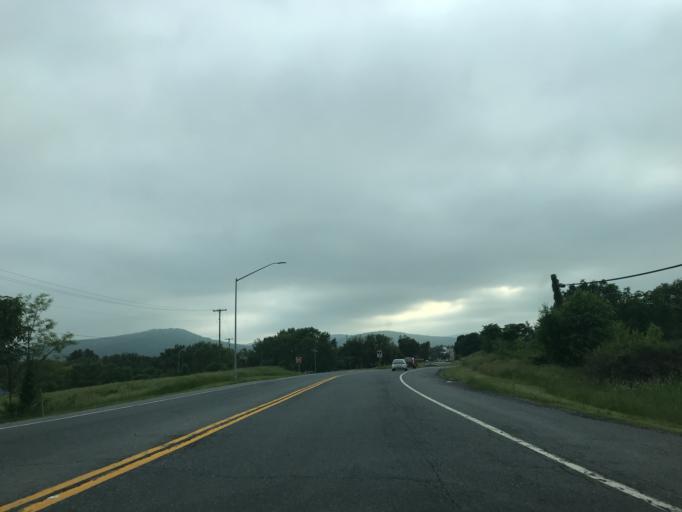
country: US
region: Maryland
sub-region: Frederick County
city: Emmitsburg
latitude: 39.7015
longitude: -77.3120
